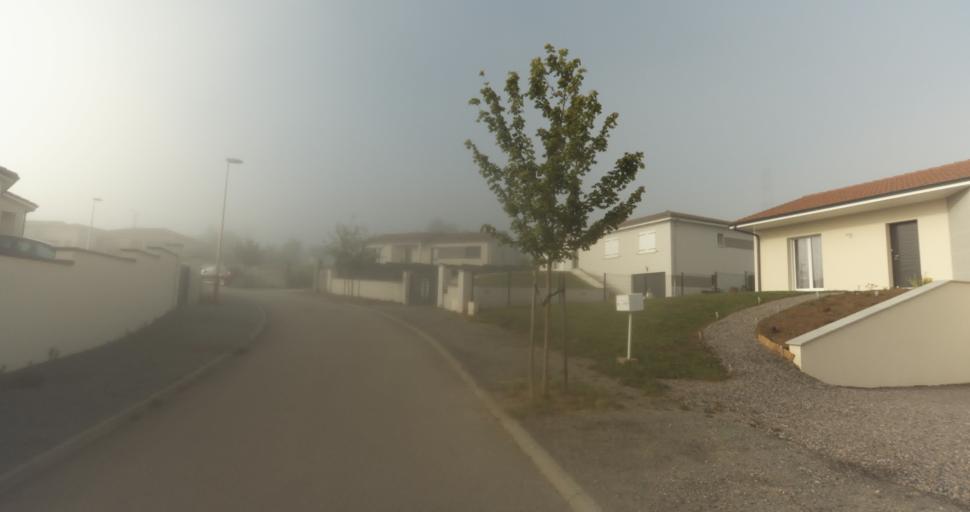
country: FR
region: Limousin
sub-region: Departement de la Haute-Vienne
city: Condat-sur-Vienne
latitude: 45.7833
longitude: 1.2773
